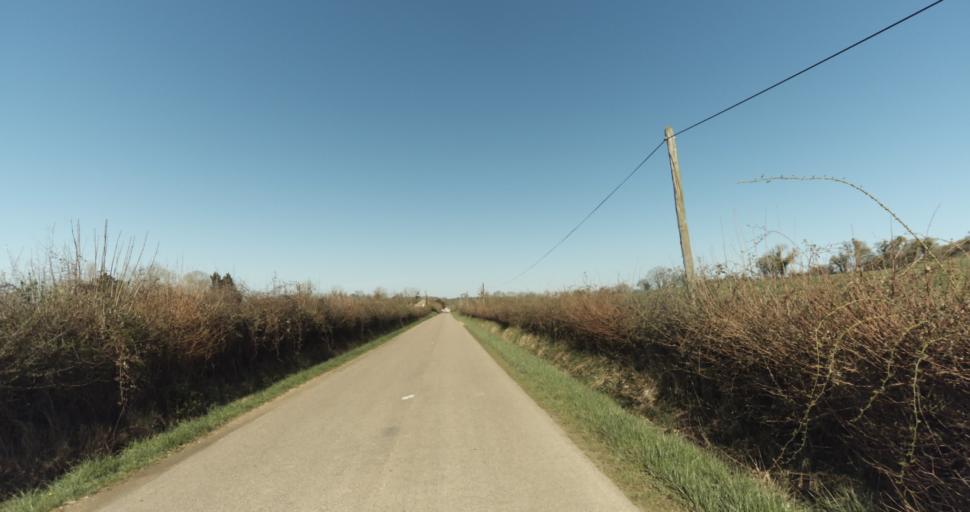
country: FR
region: Lower Normandy
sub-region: Departement du Calvados
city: Saint-Pierre-sur-Dives
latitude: 48.9720
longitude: 0.0451
